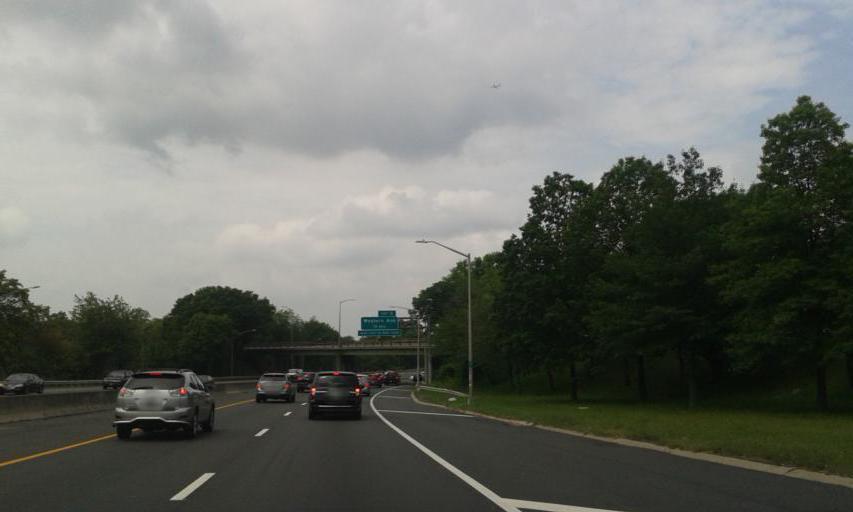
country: US
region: New York
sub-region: Richmond County
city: Bloomfield
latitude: 40.6216
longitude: -74.1714
